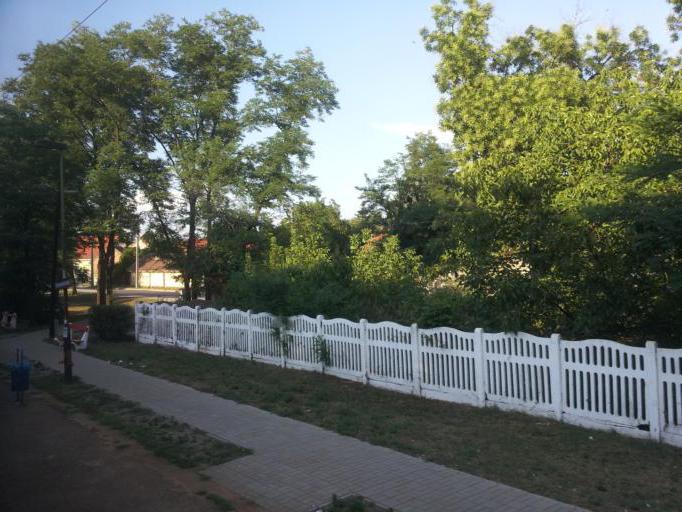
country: HU
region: Pest
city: Dunavarsany
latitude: 47.2748
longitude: 19.0648
